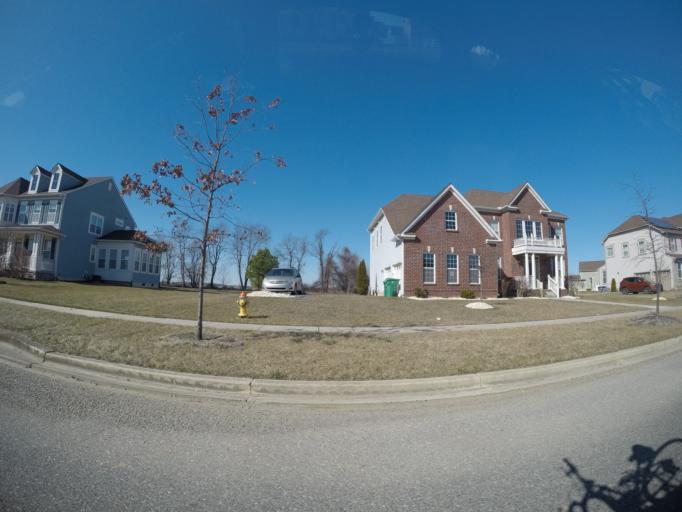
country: US
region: Delaware
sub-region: New Castle County
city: Middletown
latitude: 39.5080
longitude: -75.6667
